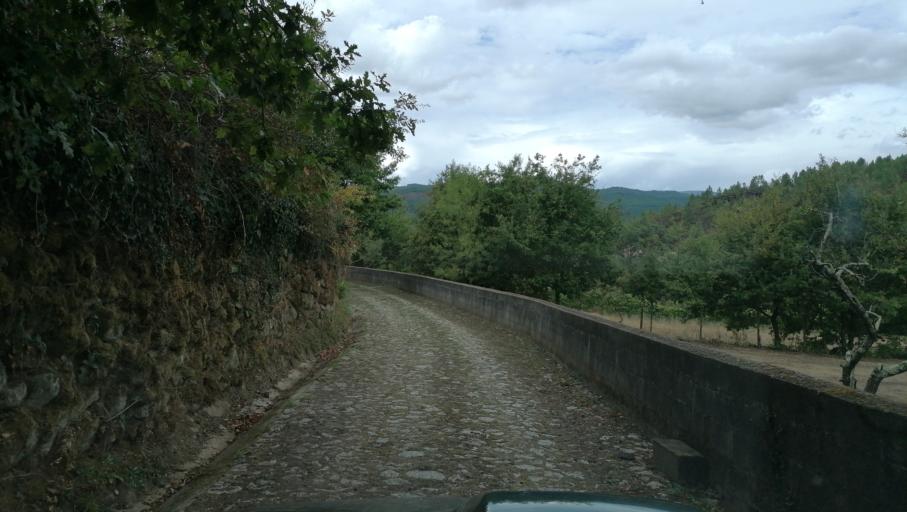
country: PT
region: Vila Real
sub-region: Ribeira de Pena
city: Sobreira
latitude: 41.5642
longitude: -7.7210
